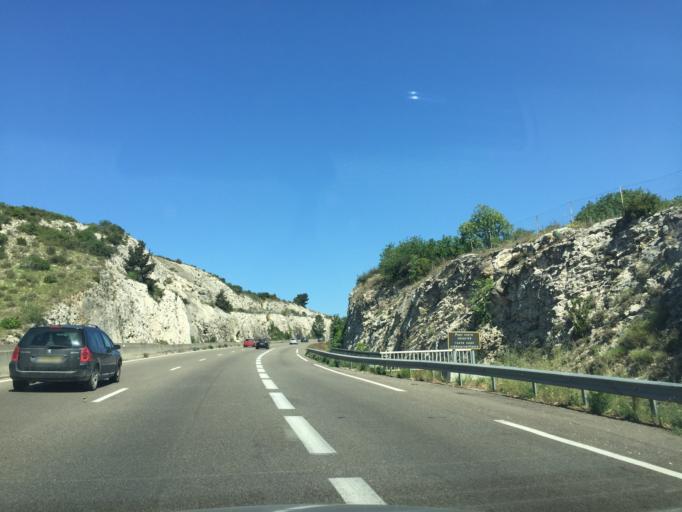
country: FR
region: Languedoc-Roussillon
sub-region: Departement du Gard
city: Les Angles
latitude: 43.9510
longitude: 4.7595
